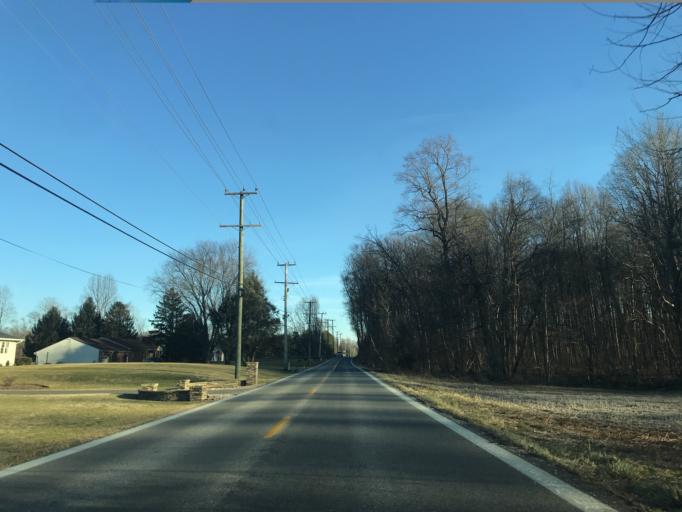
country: US
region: Maryland
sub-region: Anne Arundel County
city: Davidsonville
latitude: 38.8376
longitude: -76.6264
